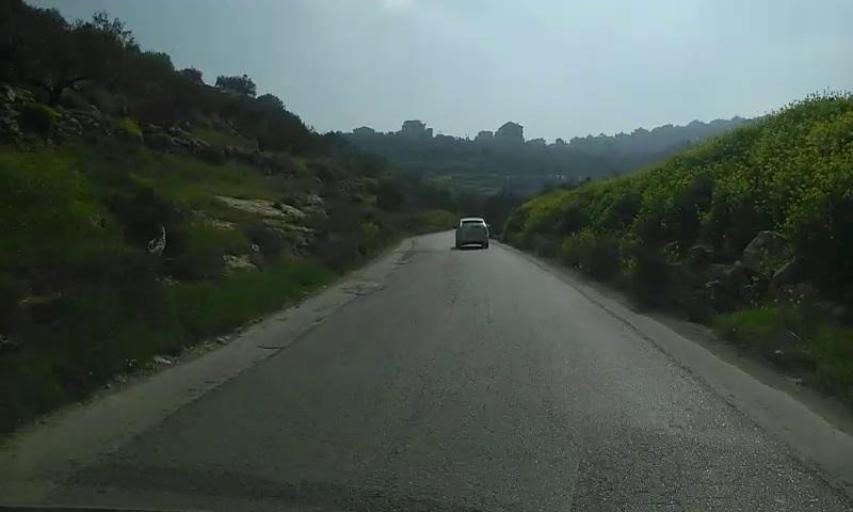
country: PS
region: West Bank
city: `Ayn Yabrud
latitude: 31.9516
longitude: 35.2412
